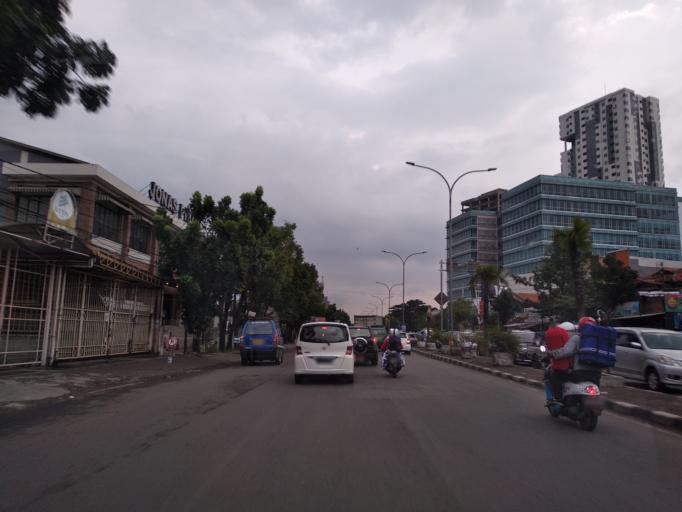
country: ID
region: West Java
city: Bandung
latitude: -6.9525
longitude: 107.6377
